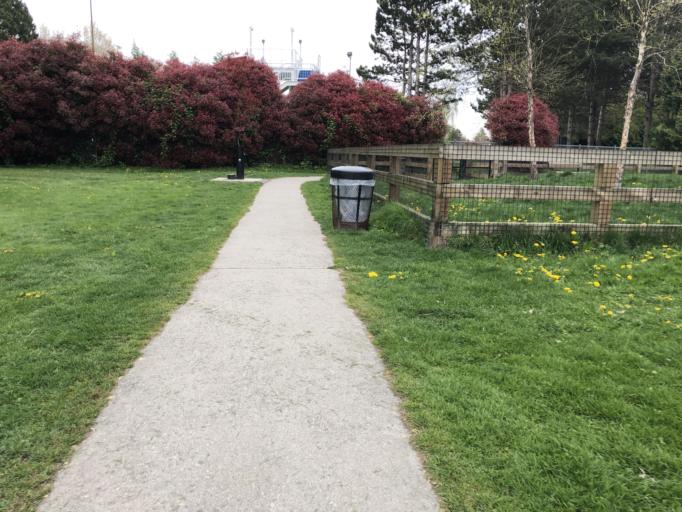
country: CA
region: British Columbia
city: Richmond
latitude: 49.1390
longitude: -123.1244
